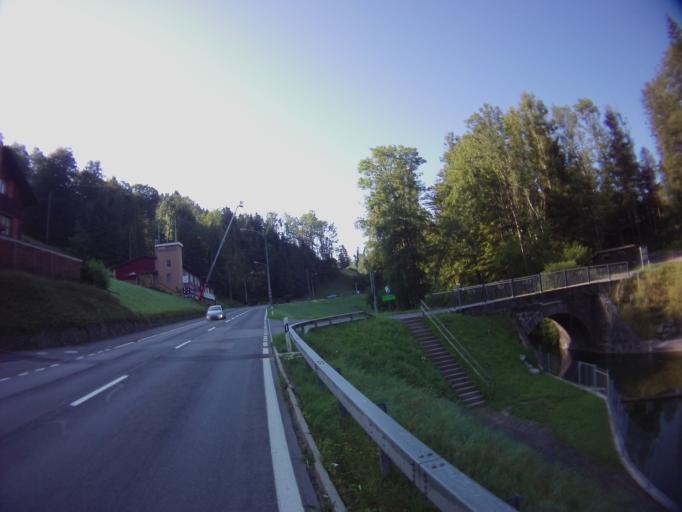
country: CH
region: Zug
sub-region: Zug
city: Unterageri
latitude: 47.1471
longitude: 8.5669
